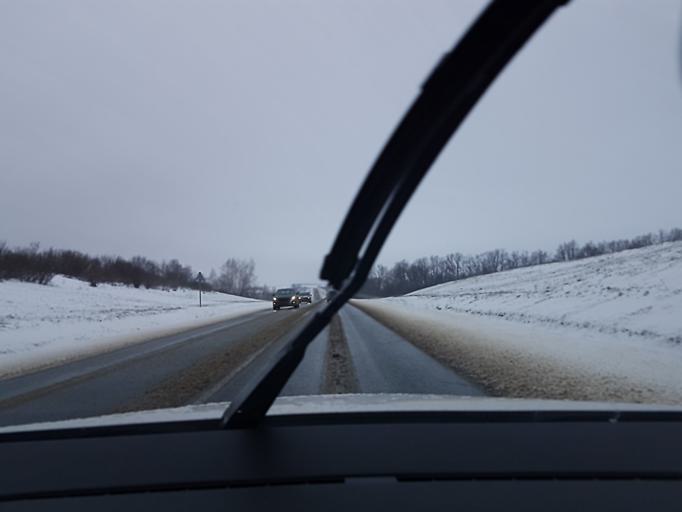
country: RU
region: Moskovskaya
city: Serebryanyye Prudy
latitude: 54.4096
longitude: 38.6642
